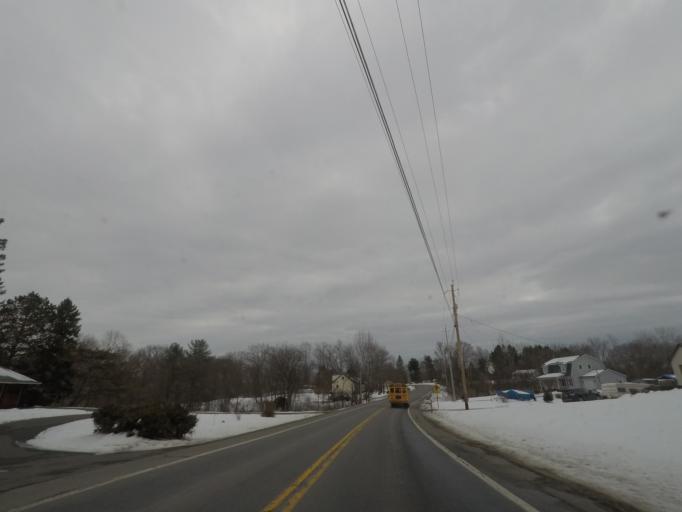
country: US
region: New York
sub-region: Saratoga County
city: Stillwater
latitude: 42.9555
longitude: -73.6710
